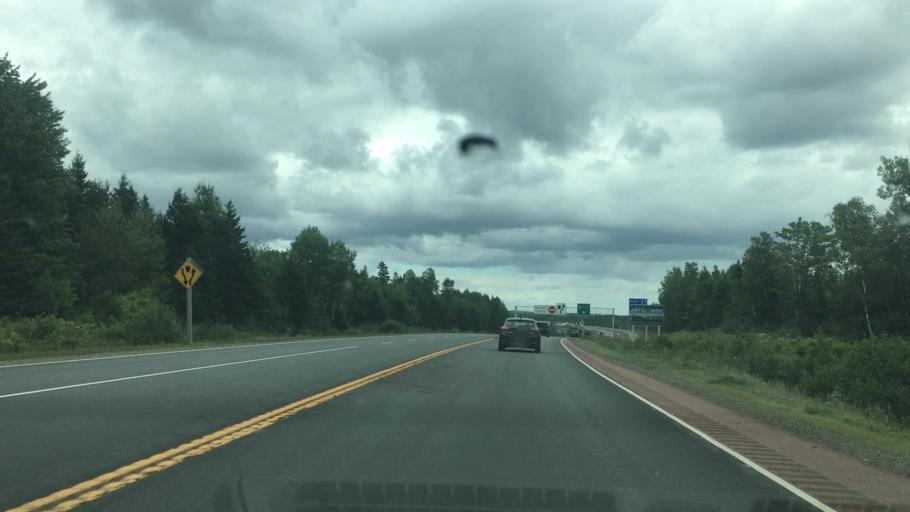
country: CA
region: Nova Scotia
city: Antigonish
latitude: 45.5966
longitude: -62.0514
